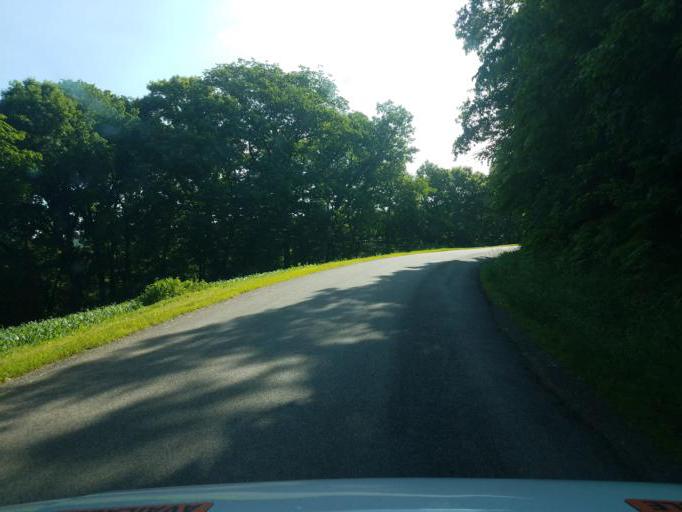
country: US
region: Wisconsin
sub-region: Sauk County
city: Reedsburg
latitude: 43.5816
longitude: -90.1452
